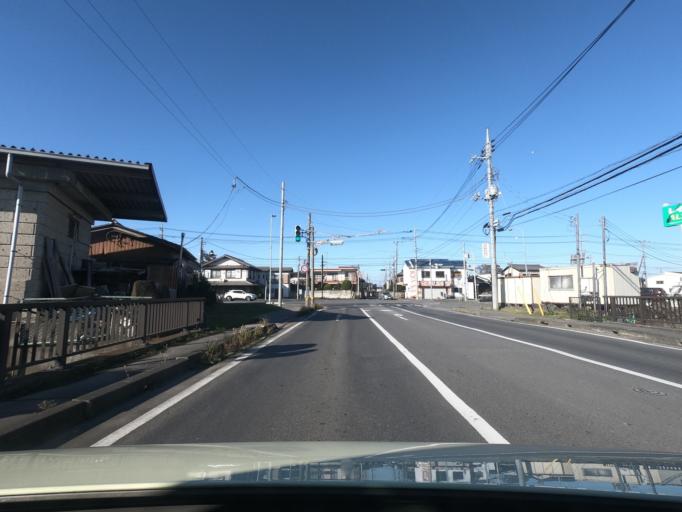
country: JP
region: Ibaraki
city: Ishige
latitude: 36.1805
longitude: 139.9729
